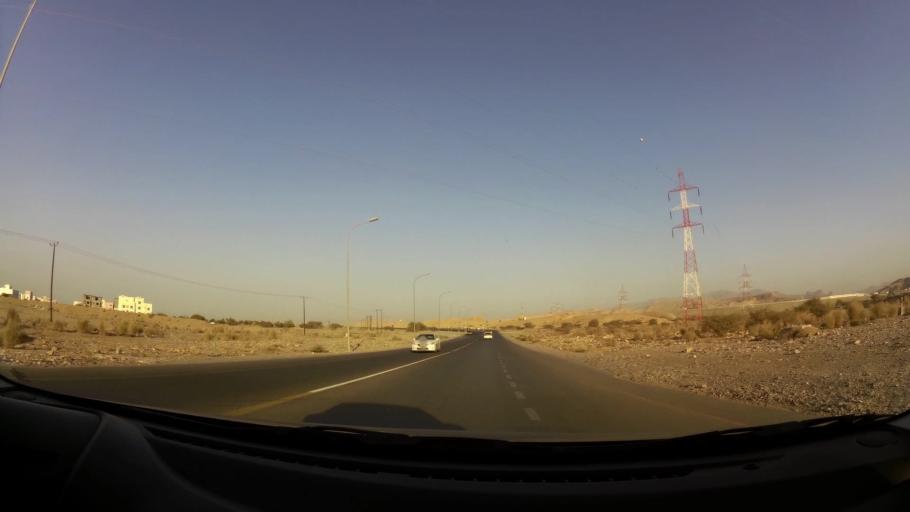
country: OM
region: Muhafazat Masqat
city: As Sib al Jadidah
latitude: 23.5744
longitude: 58.1850
